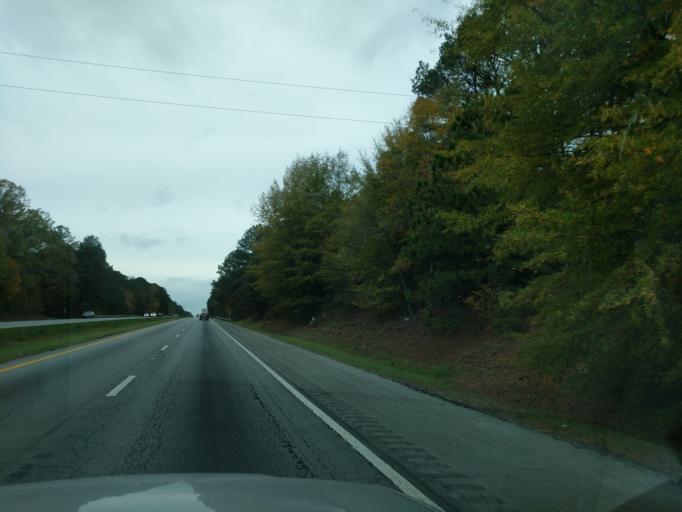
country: US
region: South Carolina
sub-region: Laurens County
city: Joanna
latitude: 34.4261
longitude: -81.7231
